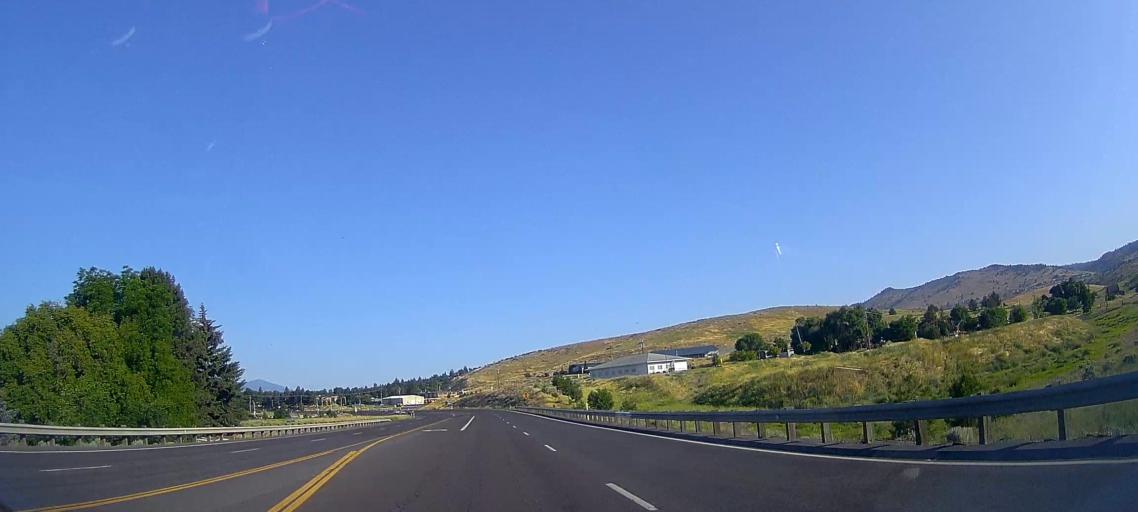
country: US
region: Oregon
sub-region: Klamath County
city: Altamont
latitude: 42.2224
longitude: -121.7530
